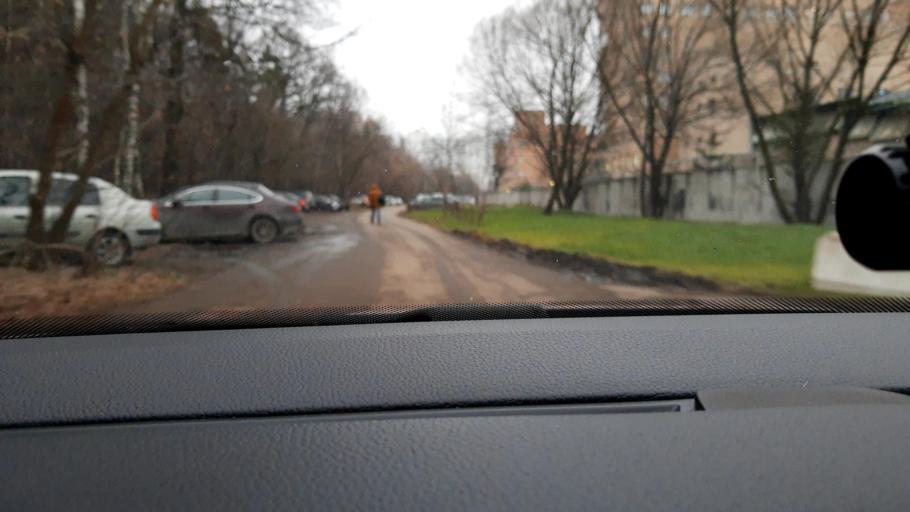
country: RU
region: Moskovskaya
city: Koptevo
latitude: 55.8172
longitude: 37.5377
